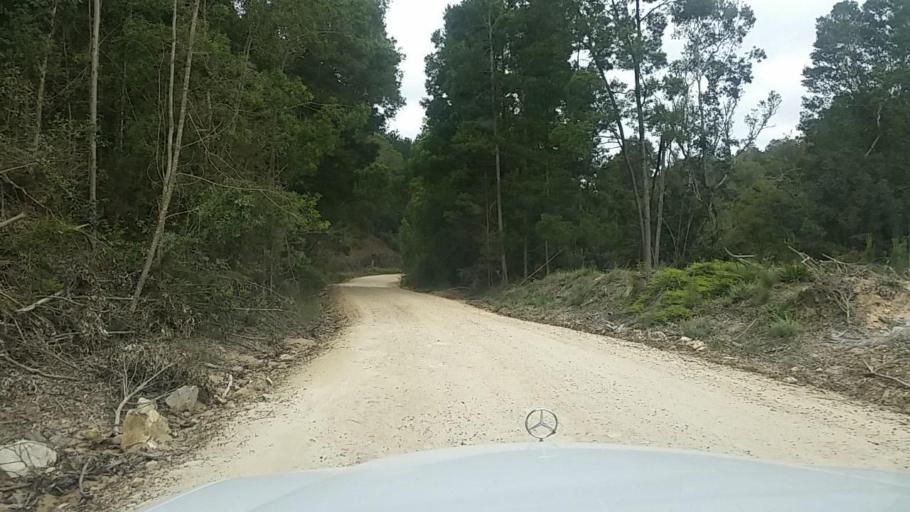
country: ZA
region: Western Cape
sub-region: Eden District Municipality
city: Knysna
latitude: -33.9995
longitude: 23.1157
